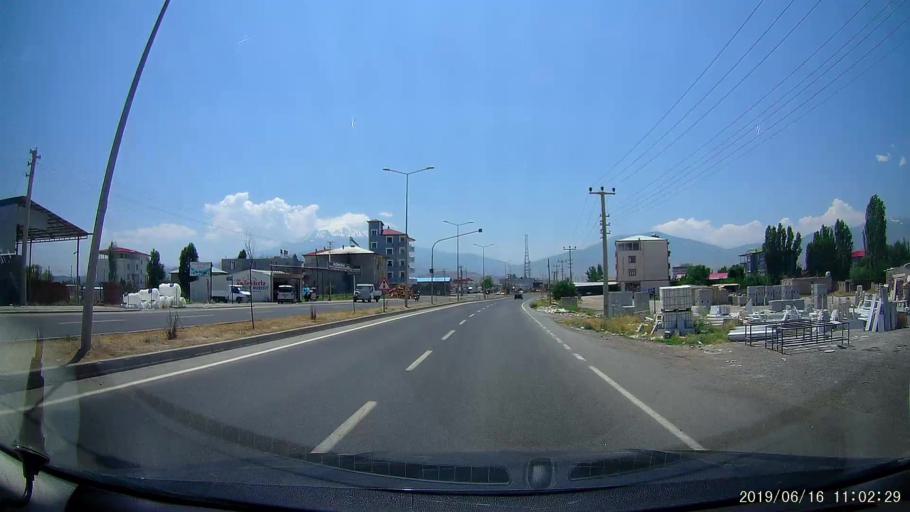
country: TR
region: Igdir
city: Igdir
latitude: 39.9065
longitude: 44.0595
